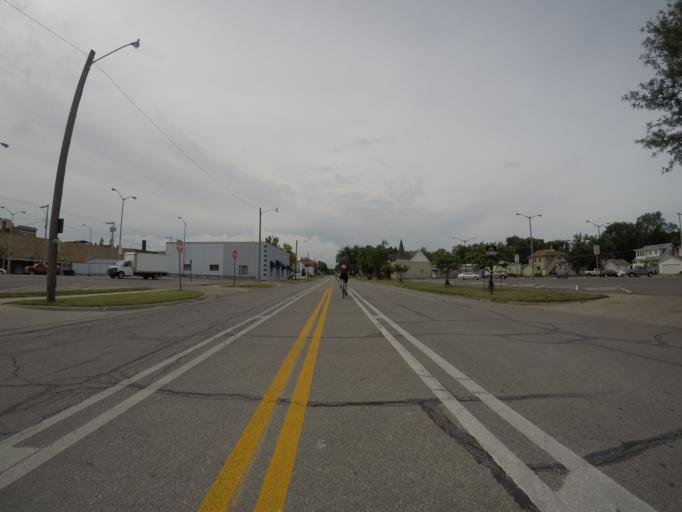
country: US
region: Kansas
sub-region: Franklin County
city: Ottawa
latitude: 38.6153
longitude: -95.2700
